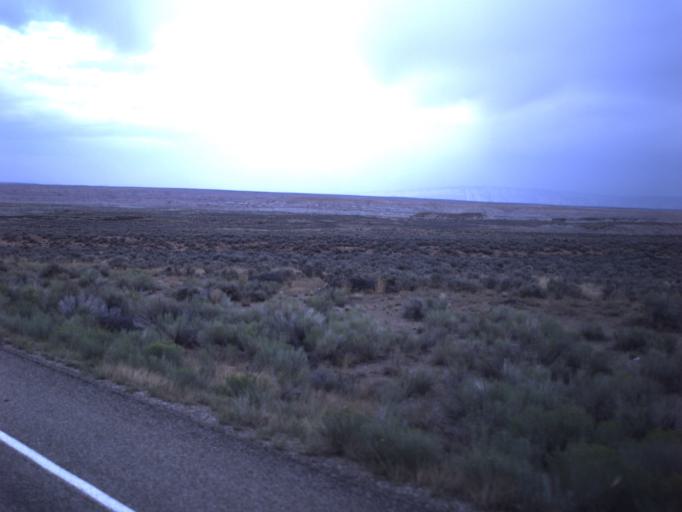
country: US
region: Colorado
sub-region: Rio Blanco County
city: Rangely
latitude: 40.0812
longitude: -109.2134
